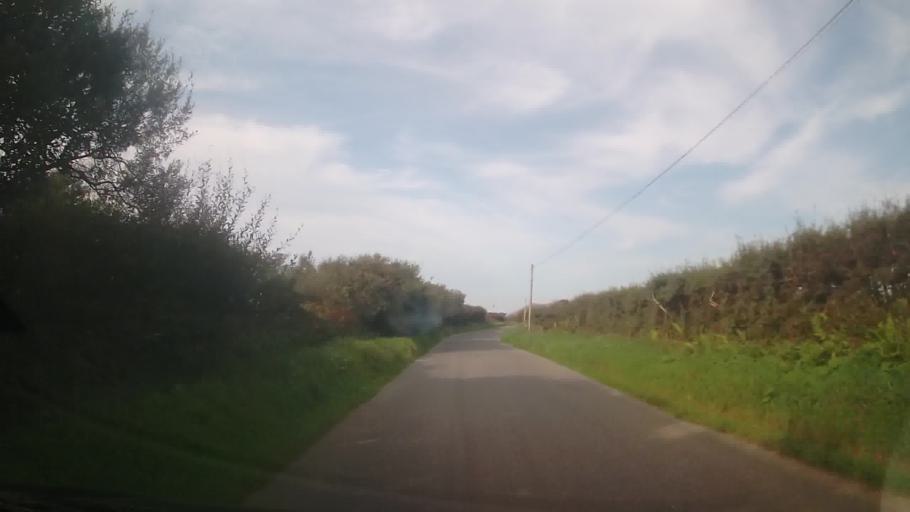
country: GB
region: Wales
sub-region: Pembrokeshire
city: Camrose
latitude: 51.8721
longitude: -5.0494
